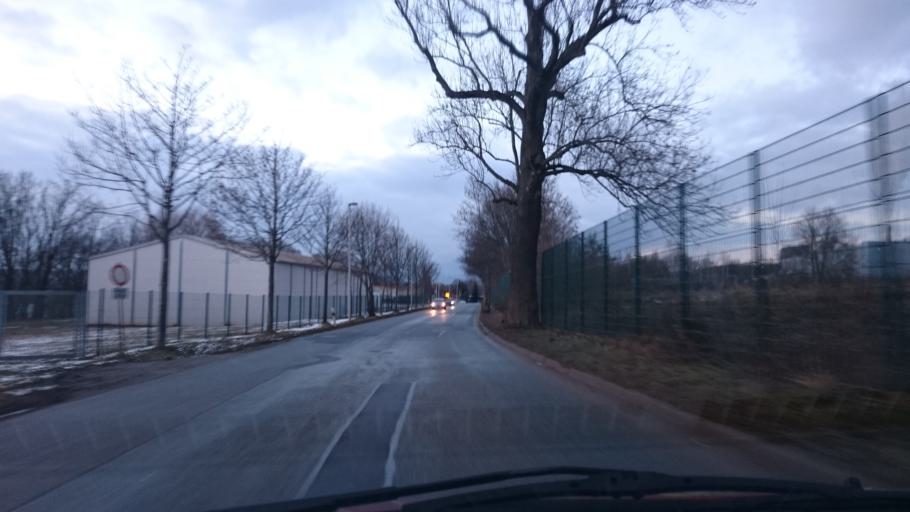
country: DE
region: Saxony
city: Zwickau
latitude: 50.7091
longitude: 12.5077
